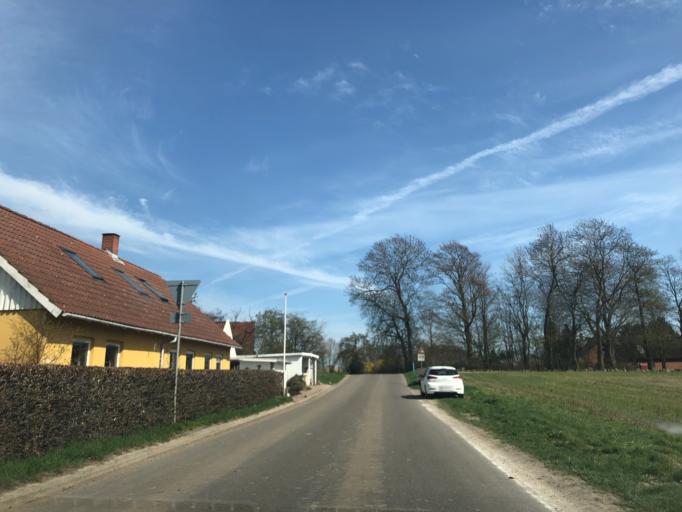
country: DK
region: Zealand
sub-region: Faxe Kommune
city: Ronnede
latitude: 55.3017
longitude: 12.0469
